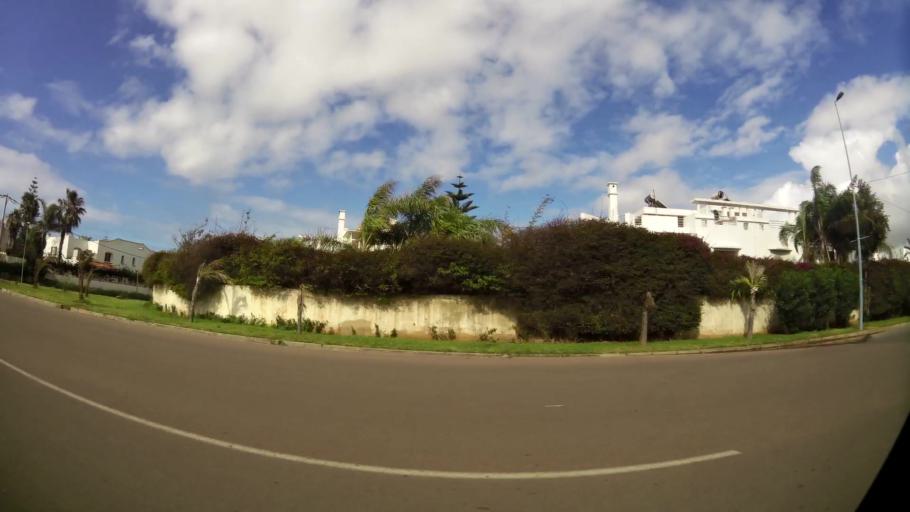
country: MA
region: Grand Casablanca
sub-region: Casablanca
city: Casablanca
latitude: 33.5698
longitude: -7.7079
